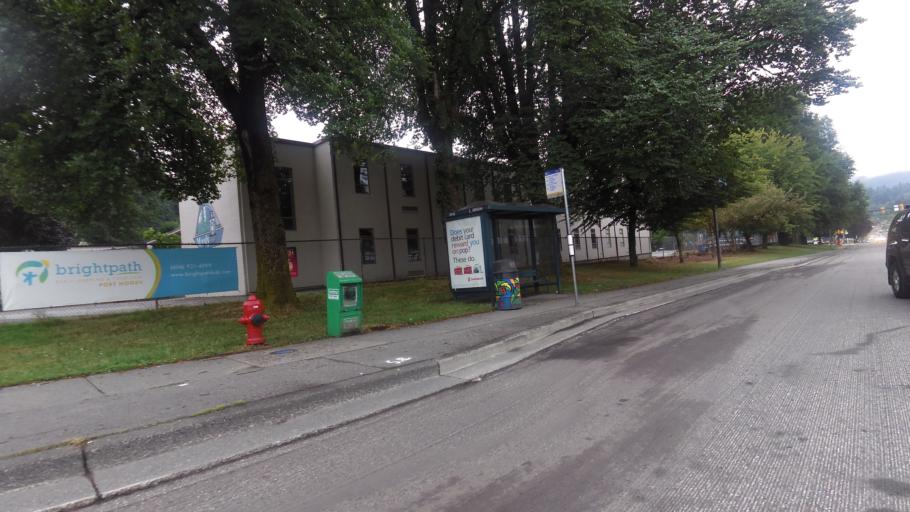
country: CA
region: British Columbia
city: Port Moody
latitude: 49.2767
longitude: -122.8504
